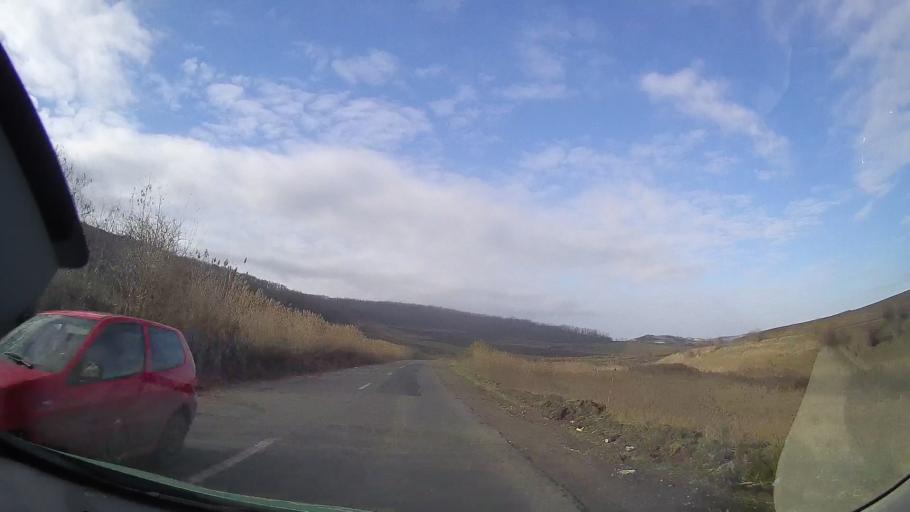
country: RO
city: Barza
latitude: 46.5547
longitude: 24.1026
